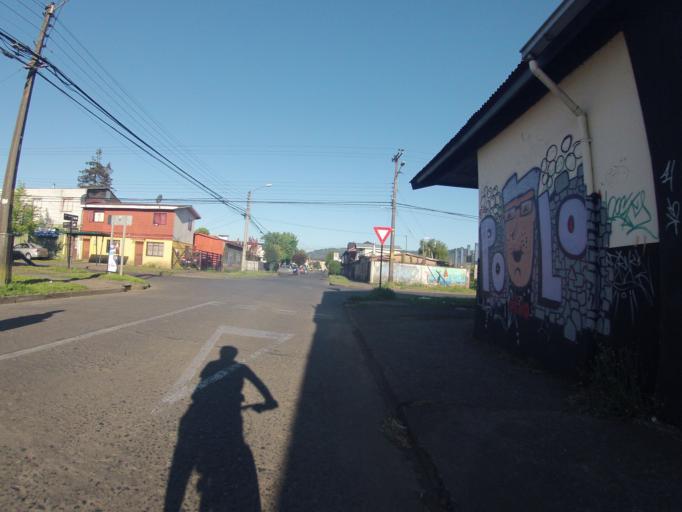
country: CL
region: Araucania
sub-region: Provincia de Cautin
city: Temuco
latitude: -38.7430
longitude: -72.6026
